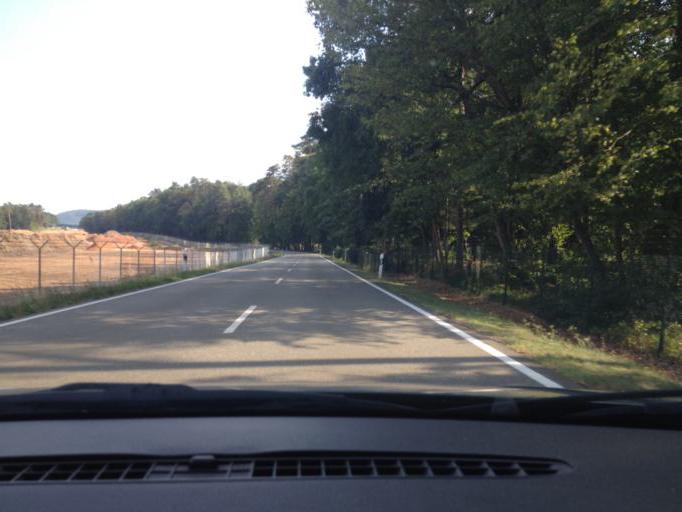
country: DE
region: Rheinland-Pfalz
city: Mackenbach
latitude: 49.4558
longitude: 7.6058
